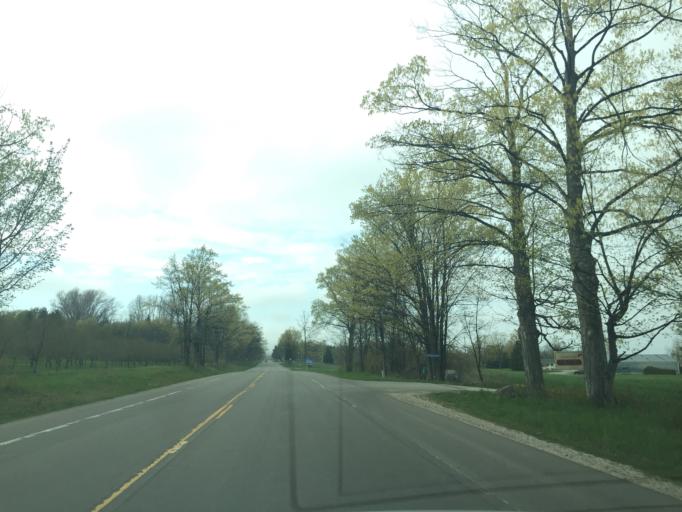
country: US
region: Michigan
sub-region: Leelanau County
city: Leland
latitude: 45.0737
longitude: -85.5890
